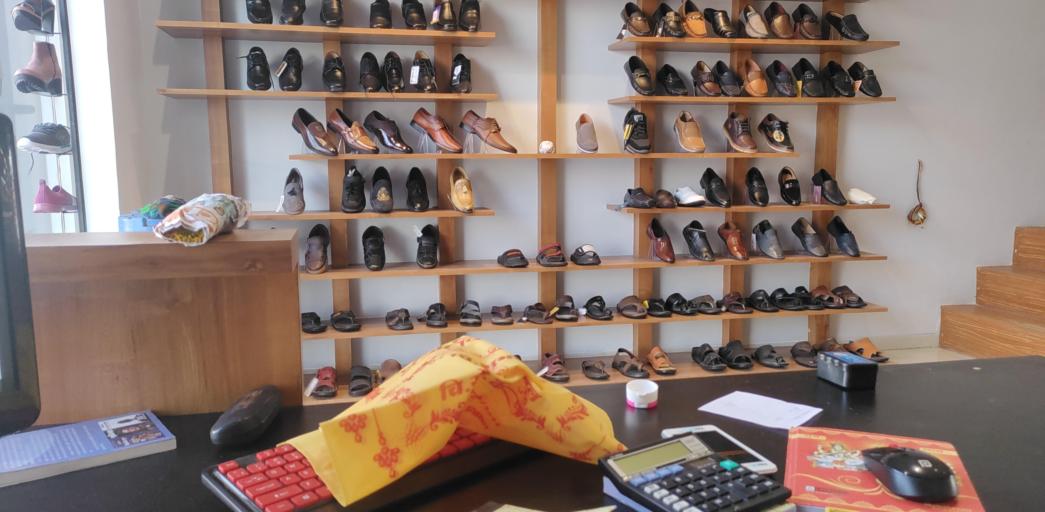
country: IN
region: Maharashtra
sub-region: Aurangabad Division
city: Aurangabad
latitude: 19.8657
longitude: 75.3672
